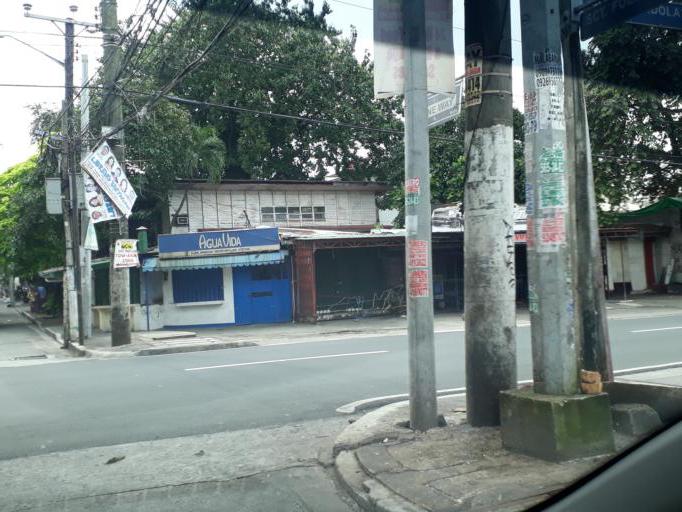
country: PH
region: Metro Manila
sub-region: Quezon City
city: Quezon City
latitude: 14.6313
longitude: 121.0389
